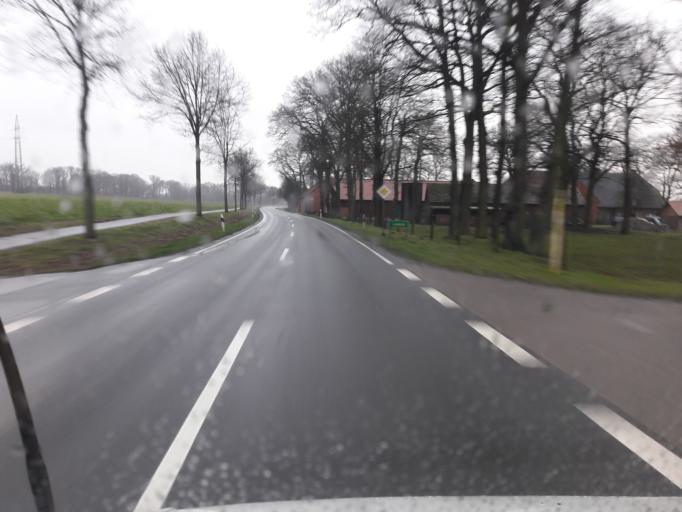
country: DE
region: Lower Saxony
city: Uchte
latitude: 52.4865
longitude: 8.8855
